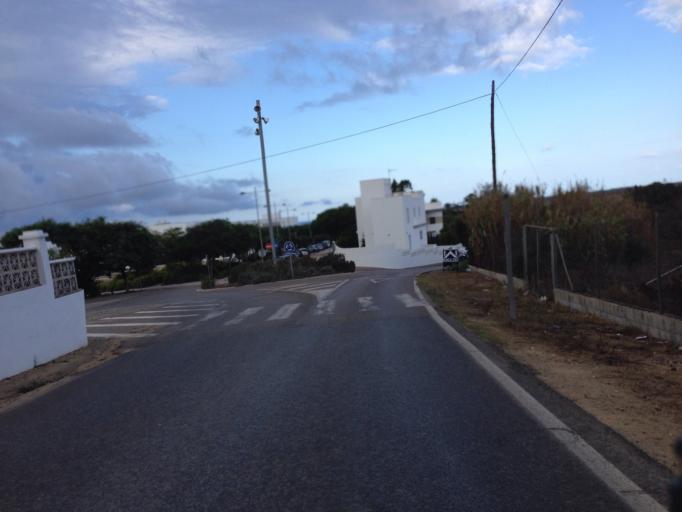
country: ES
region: Andalusia
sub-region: Provincia de Cadiz
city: Conil de la Frontera
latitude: 36.2890
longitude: -6.1029
